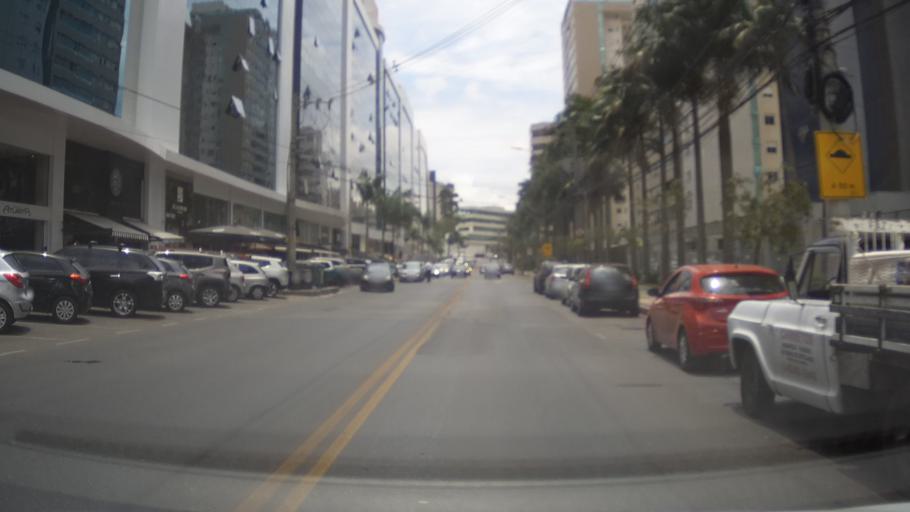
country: BR
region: Minas Gerais
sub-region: Belo Horizonte
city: Belo Horizonte
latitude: -19.9772
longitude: -43.9410
